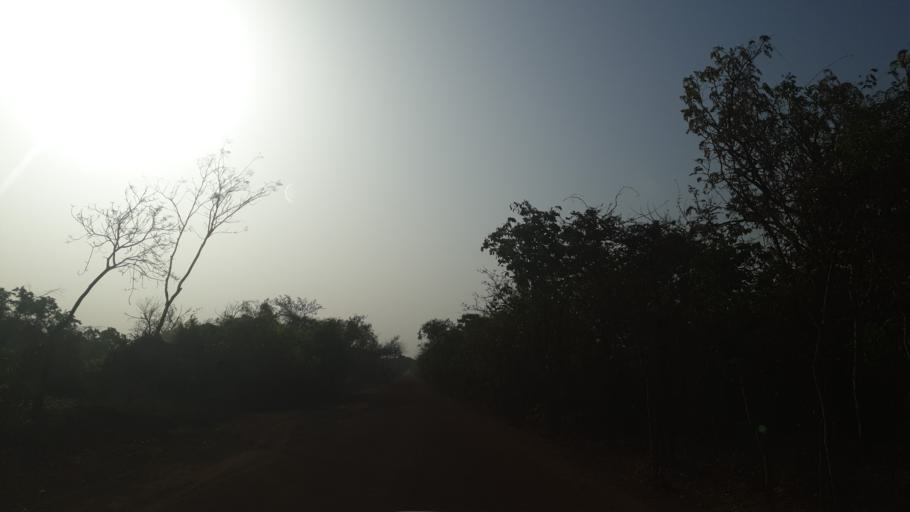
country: ML
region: Sikasso
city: Kolondieba
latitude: 10.8978
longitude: -6.8875
